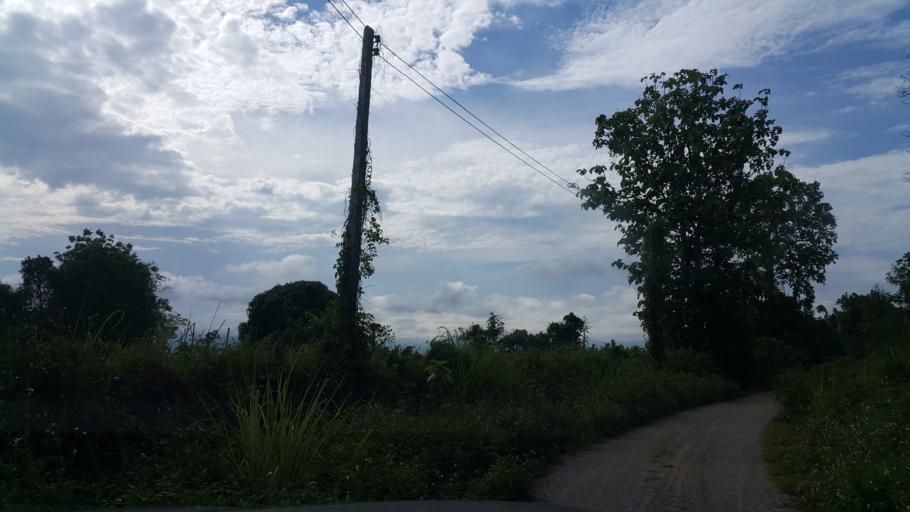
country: TH
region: Chiang Rai
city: Wiang Chai
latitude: 19.9703
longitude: 99.9192
